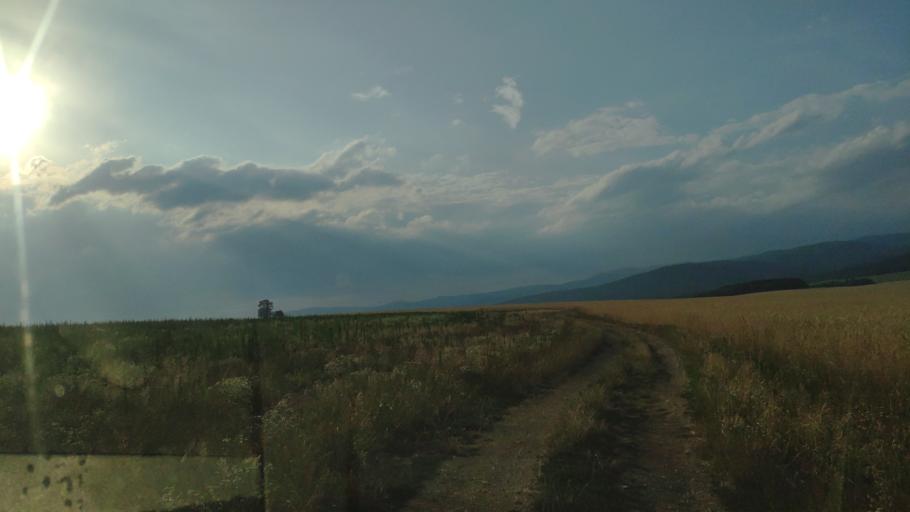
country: SK
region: Kosicky
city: Moldava nad Bodvou
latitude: 48.6936
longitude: 20.9982
